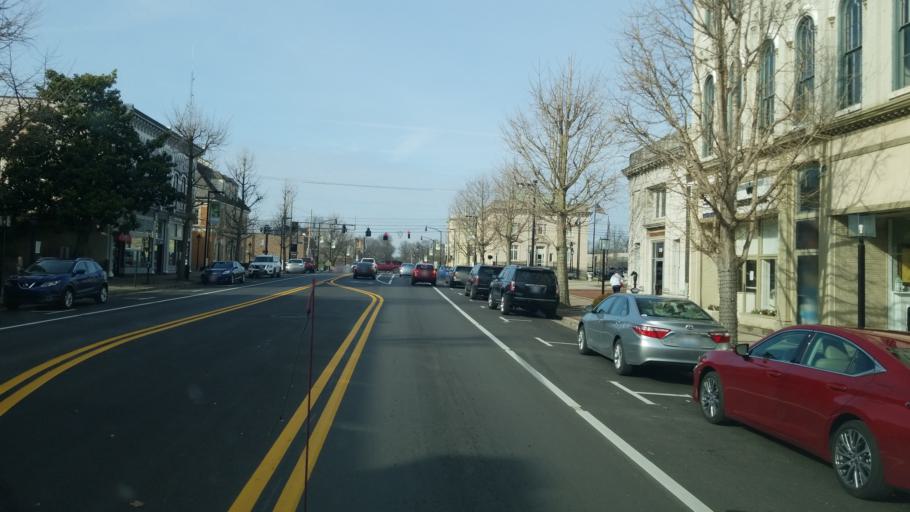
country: US
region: Kentucky
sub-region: Boyle County
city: Danville
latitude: 37.6459
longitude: -84.7729
